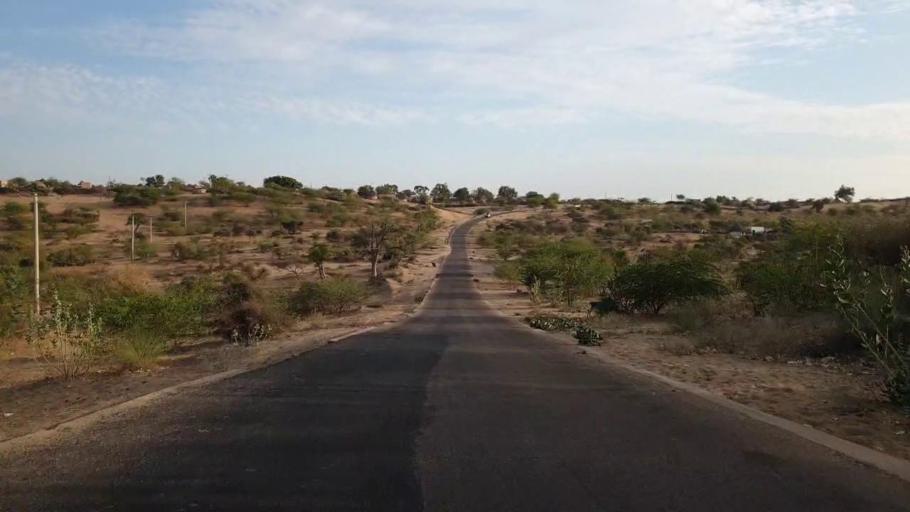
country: PK
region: Sindh
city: Umarkot
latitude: 25.1578
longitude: 70.0107
